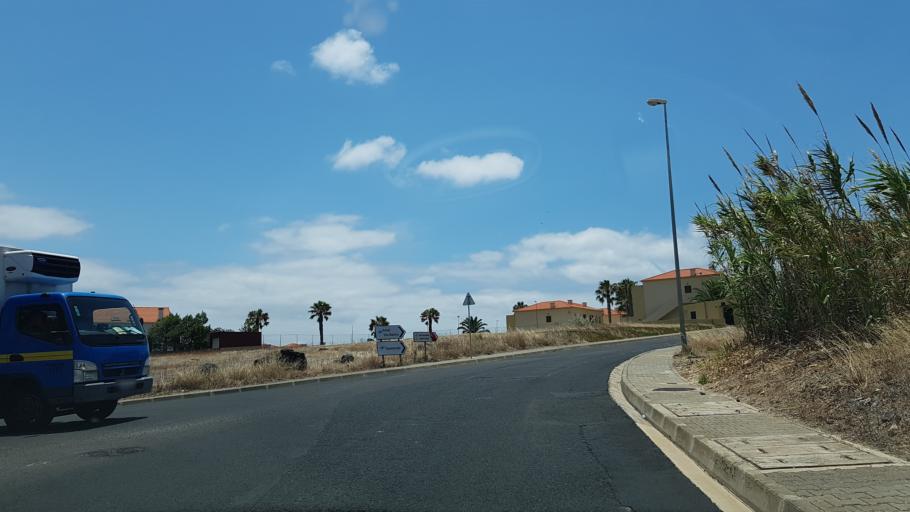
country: PT
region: Madeira
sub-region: Porto Santo
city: Vila de Porto Santo
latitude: 33.0579
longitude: -16.3412
